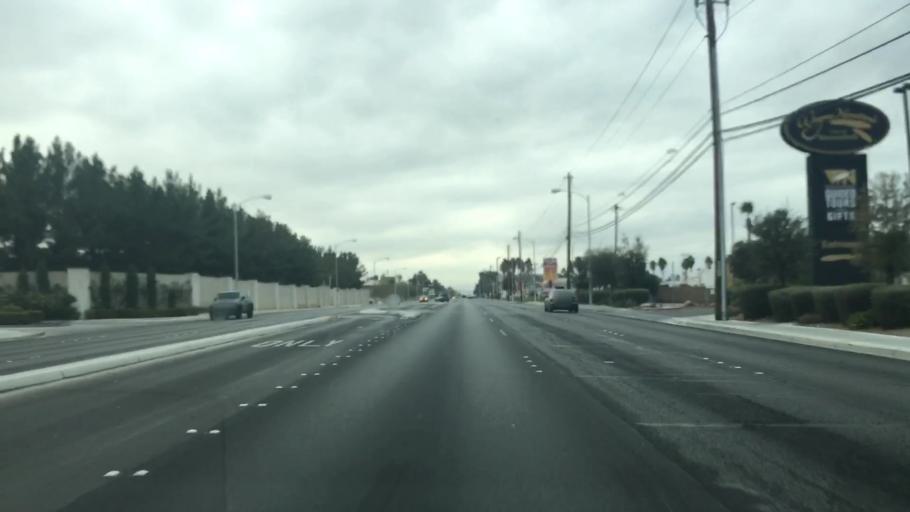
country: US
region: Nevada
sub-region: Clark County
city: Whitney
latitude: 36.0716
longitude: -115.1030
